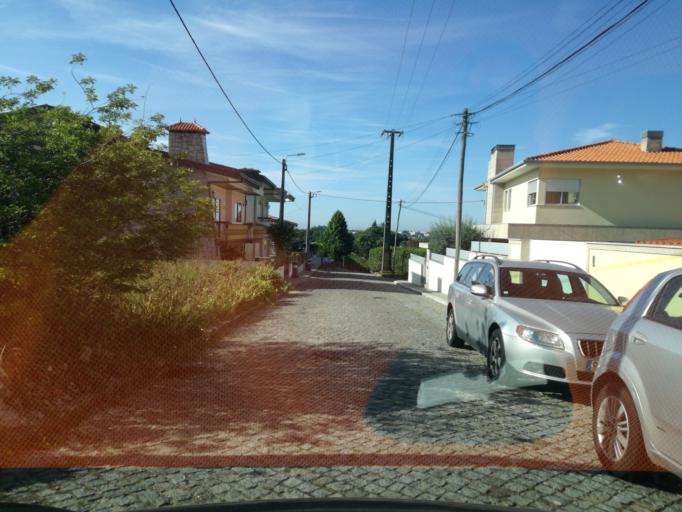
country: PT
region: Porto
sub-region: Maia
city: Anta
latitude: 41.2855
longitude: -8.6108
